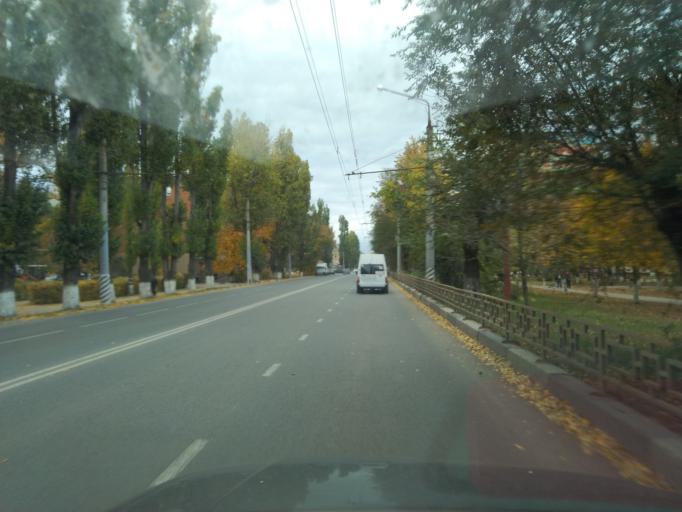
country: RU
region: Saratov
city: Engel's
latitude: 51.4760
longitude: 46.1308
